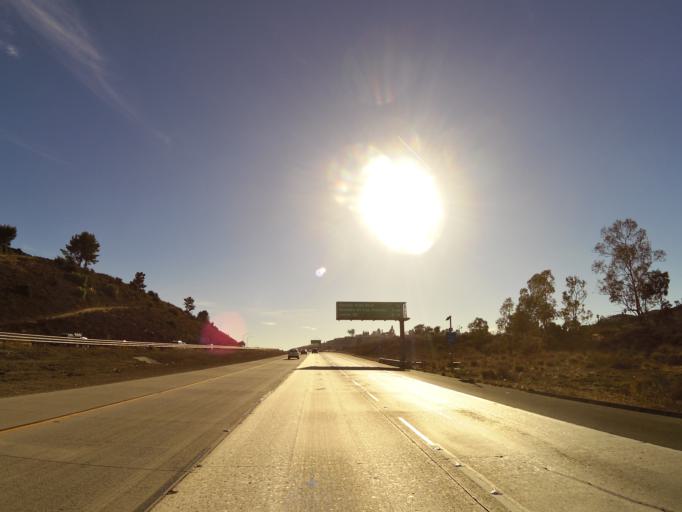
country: US
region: California
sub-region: Ventura County
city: Moorpark
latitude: 34.2347
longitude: -118.8430
